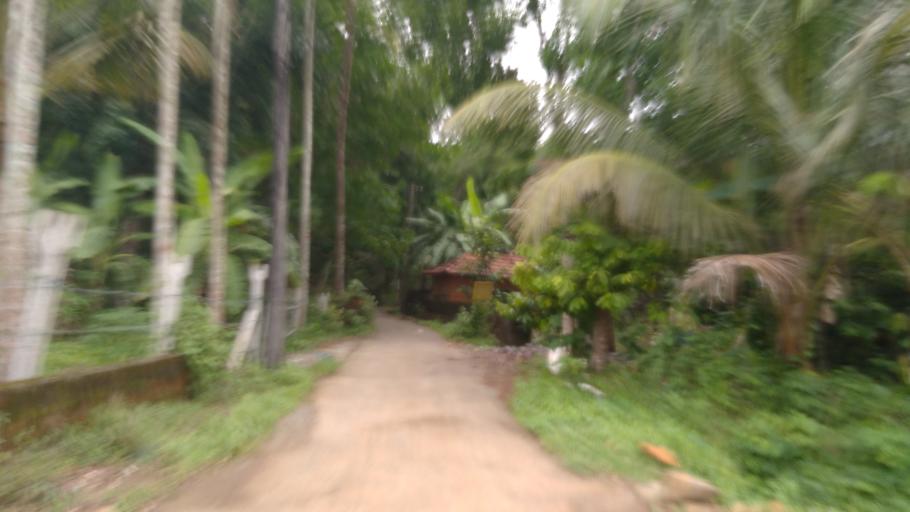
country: IN
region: Kerala
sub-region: Ernakulam
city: Kotamangalam
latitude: 10.1239
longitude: 76.5798
